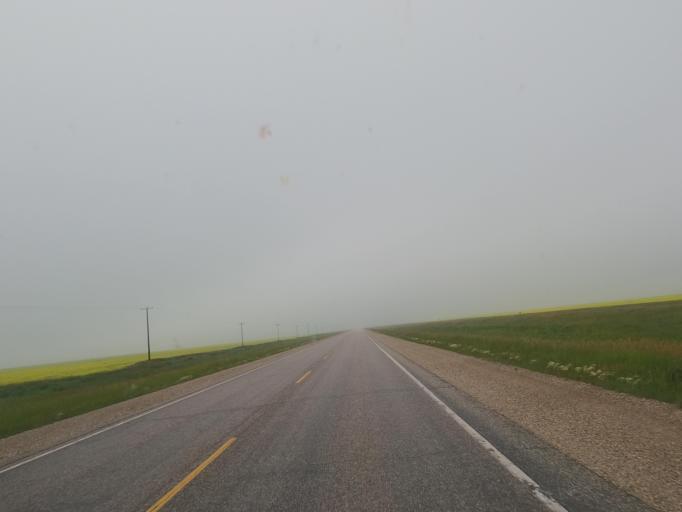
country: CA
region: Manitoba
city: Carman
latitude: 49.7080
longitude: -97.9261
